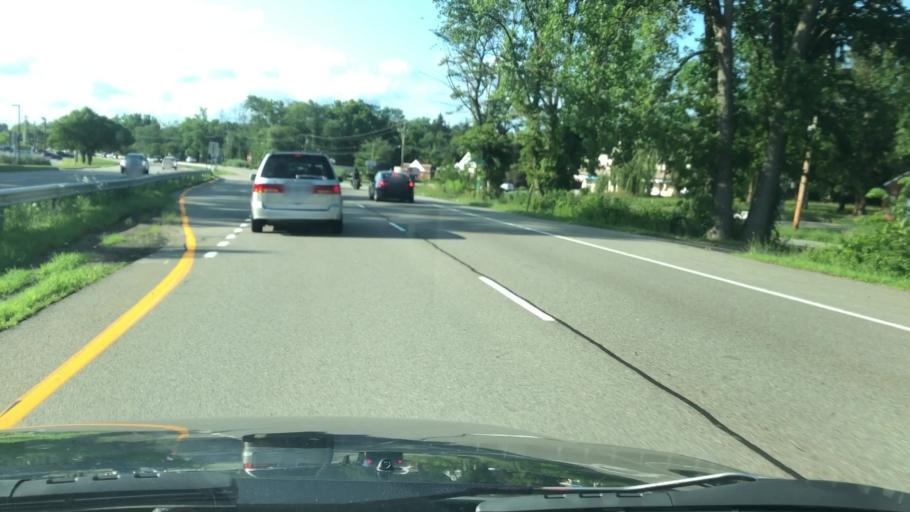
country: US
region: New York
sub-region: Dutchess County
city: Fishkill
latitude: 41.5602
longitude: -73.9034
